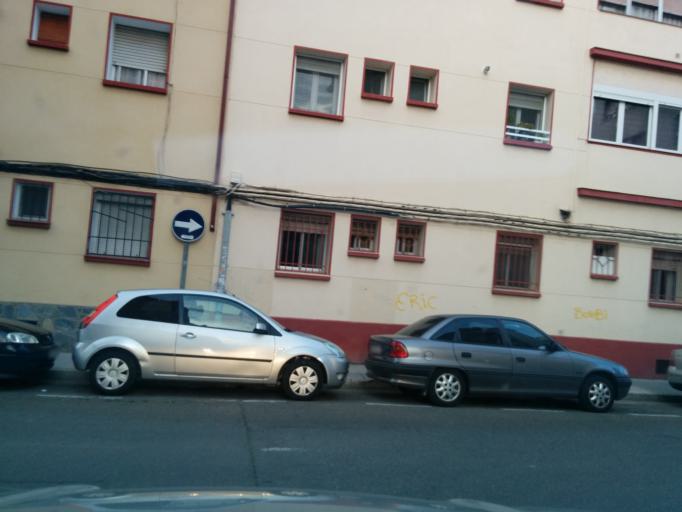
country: ES
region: Aragon
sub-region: Provincia de Zaragoza
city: Zaragoza
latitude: 41.6363
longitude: -0.8724
